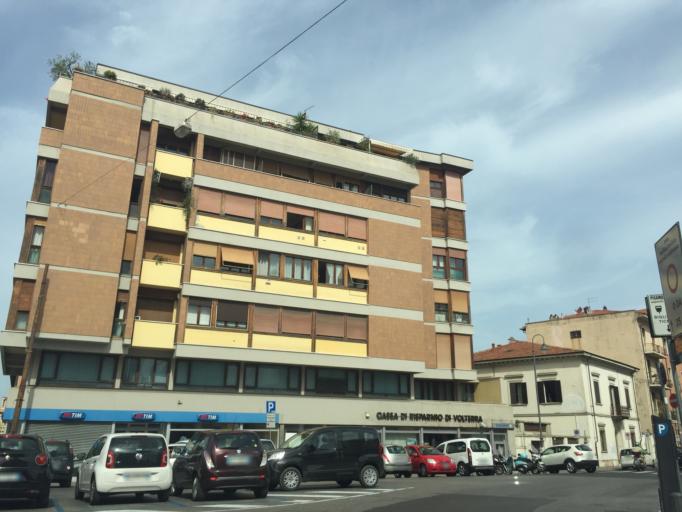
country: IT
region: Tuscany
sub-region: Province of Pisa
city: Pisa
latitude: 43.7110
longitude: 10.3975
